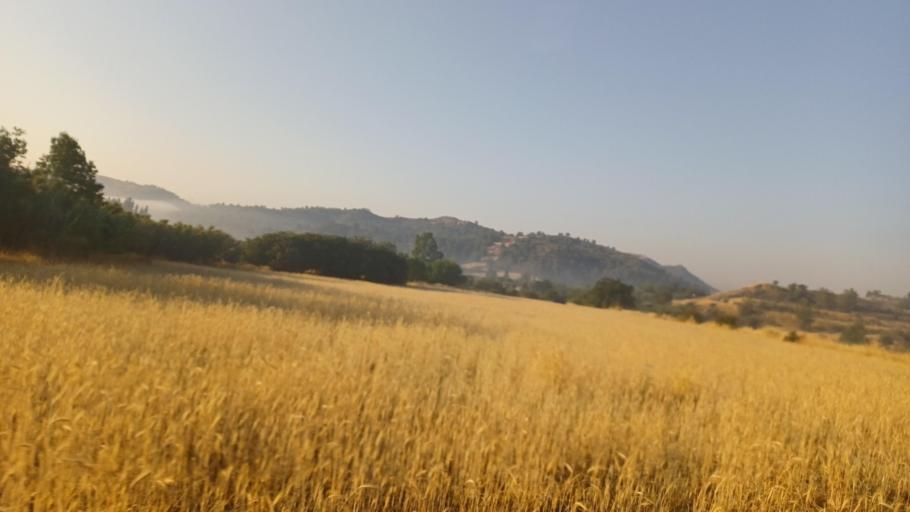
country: CY
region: Larnaka
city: Mosfiloti
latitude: 34.9732
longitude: 33.4278
